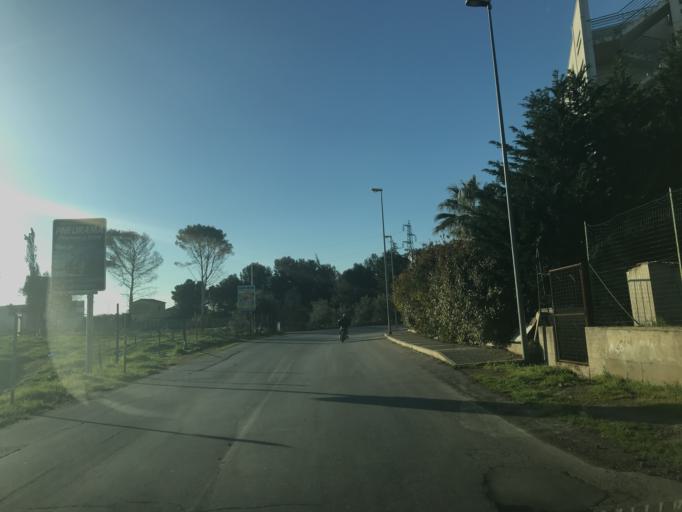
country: IT
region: Apulia
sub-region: Provincia di Bari
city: Corato
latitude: 41.1412
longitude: 16.4154
